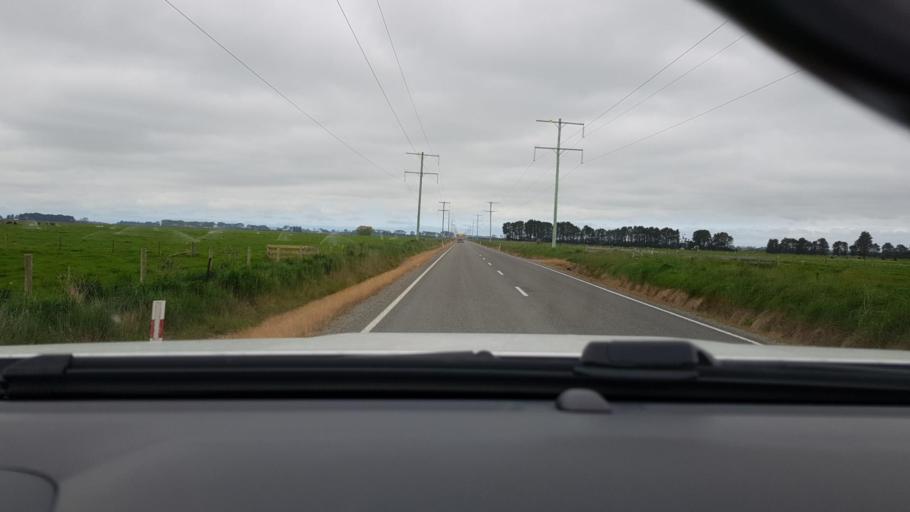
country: NZ
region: Otago
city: Oamaru
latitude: -44.9647
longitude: 170.9839
